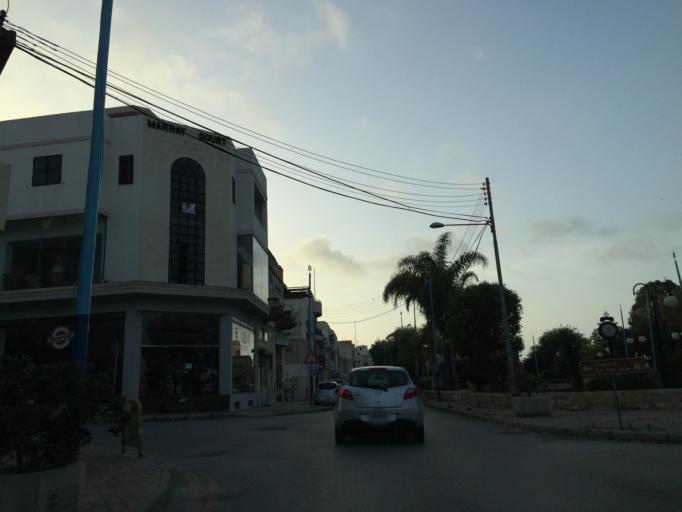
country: MT
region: Saint Paul's Bay
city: San Pawl il-Bahar
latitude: 35.9336
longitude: 14.4152
